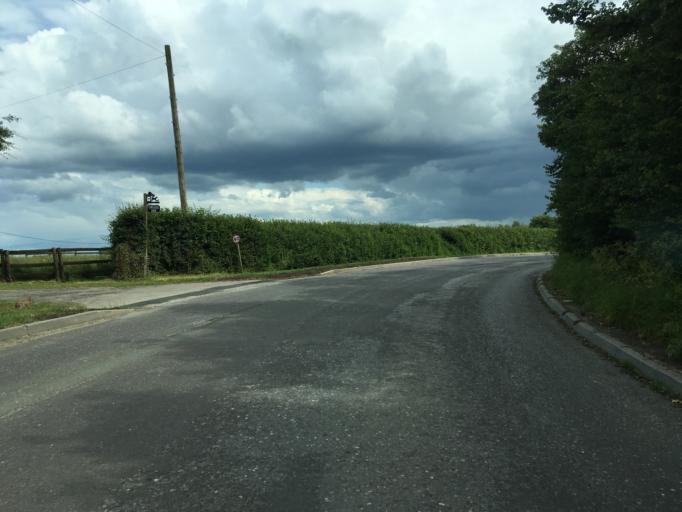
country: GB
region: England
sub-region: Wiltshire
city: Cricklade
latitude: 51.6330
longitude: -1.8793
